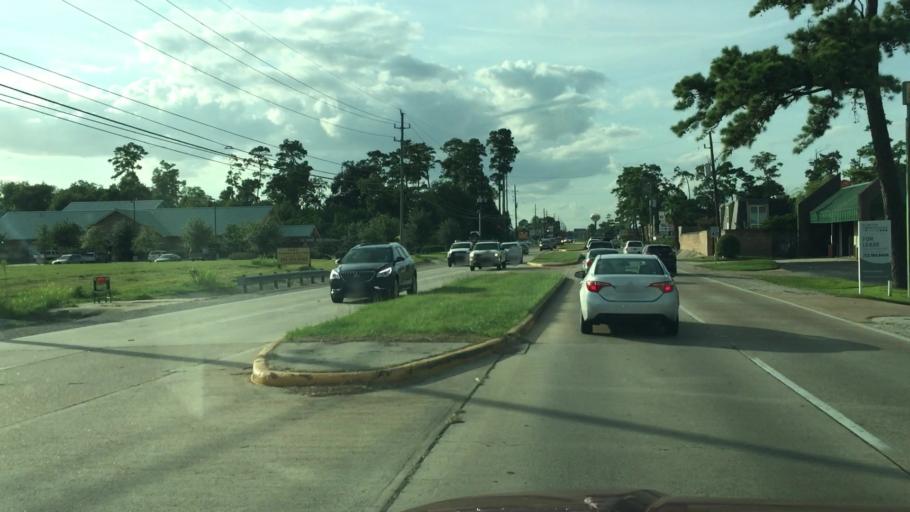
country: US
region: Texas
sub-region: Harris County
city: Hudson
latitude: 30.0121
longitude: -95.5159
